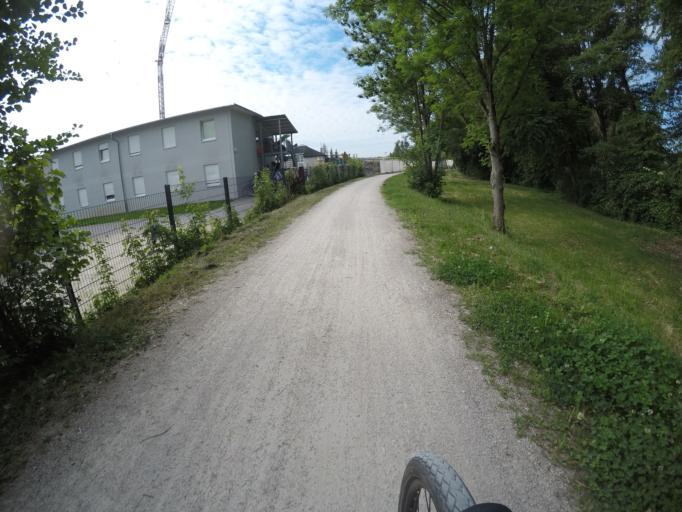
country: DE
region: Baden-Wuerttemberg
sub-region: Regierungsbezirk Stuttgart
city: Oberboihingen
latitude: 48.6540
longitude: 9.3641
